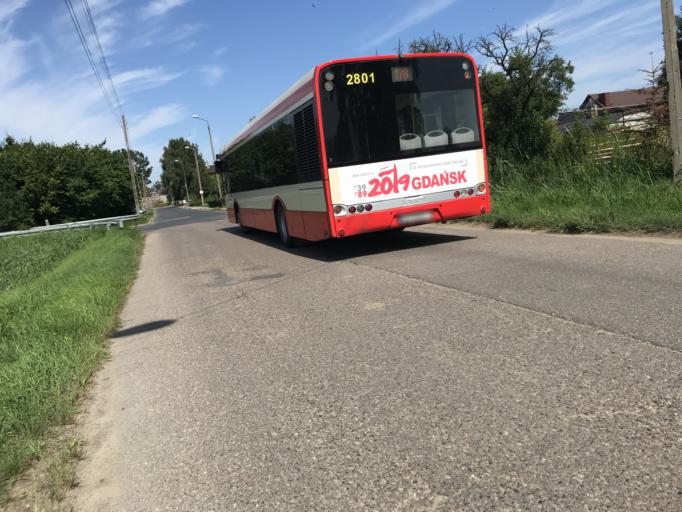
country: PL
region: Pomeranian Voivodeship
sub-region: Gdansk
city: Gdansk
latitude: 54.3343
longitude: 18.6783
